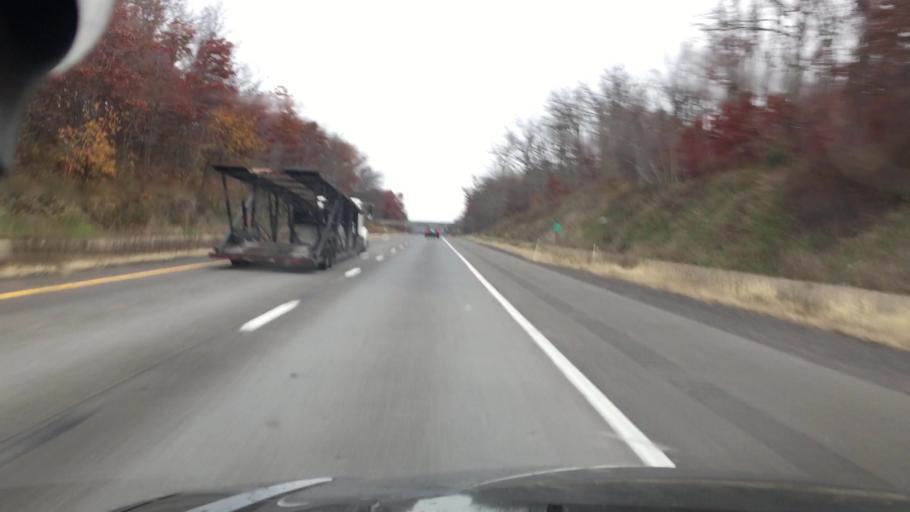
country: US
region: Pennsylvania
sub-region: Luzerne County
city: Nanticoke
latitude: 41.1182
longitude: -75.9612
